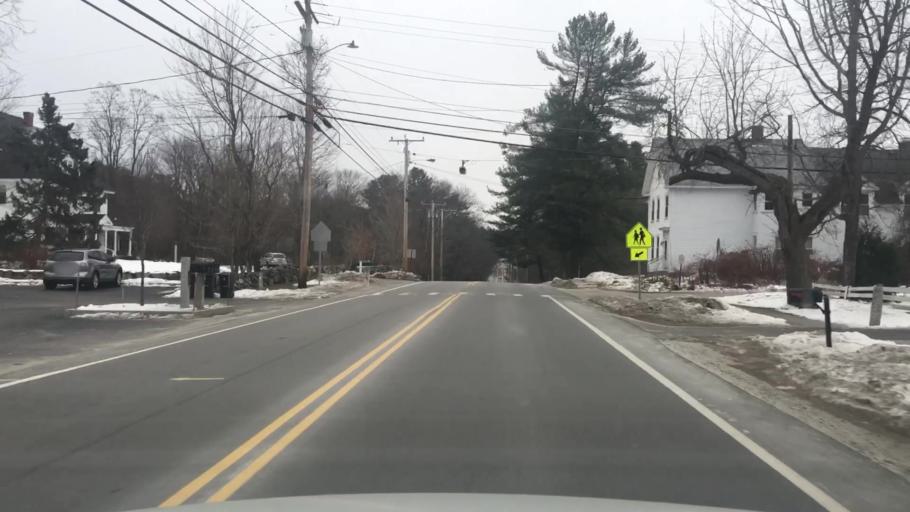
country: US
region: New Hampshire
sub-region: Merrimack County
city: Hopkinton
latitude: 43.1906
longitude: -71.6711
